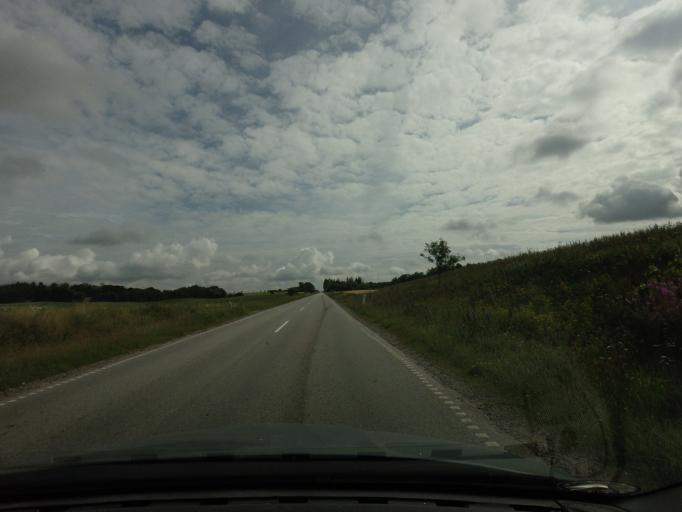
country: DK
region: North Denmark
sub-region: Bronderslev Kommune
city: Hjallerup
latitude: 57.2729
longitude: 10.1731
